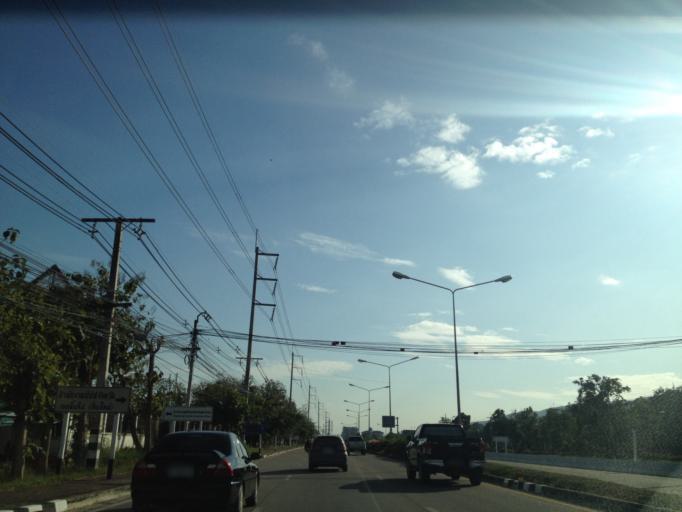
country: TH
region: Chiang Mai
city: Chiang Mai
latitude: 18.8390
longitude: 98.9650
